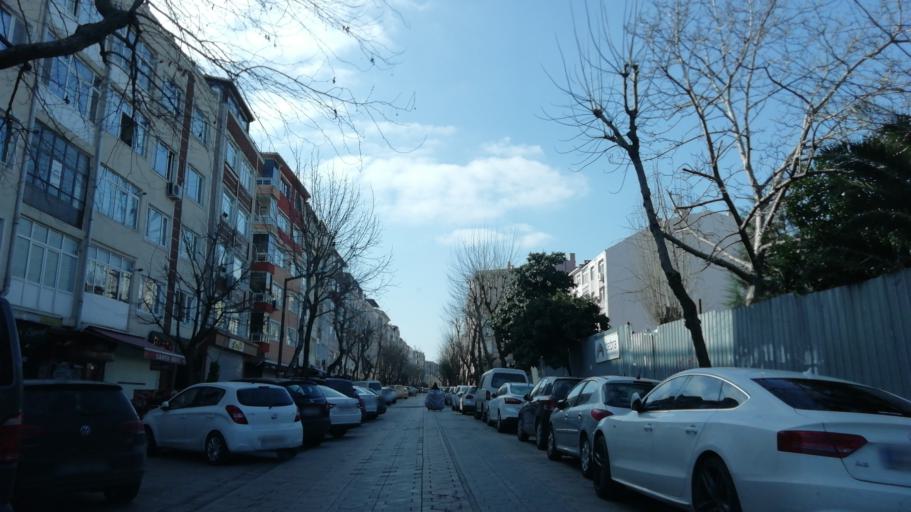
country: TR
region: Istanbul
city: guengoeren merter
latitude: 41.0071
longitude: 28.8924
